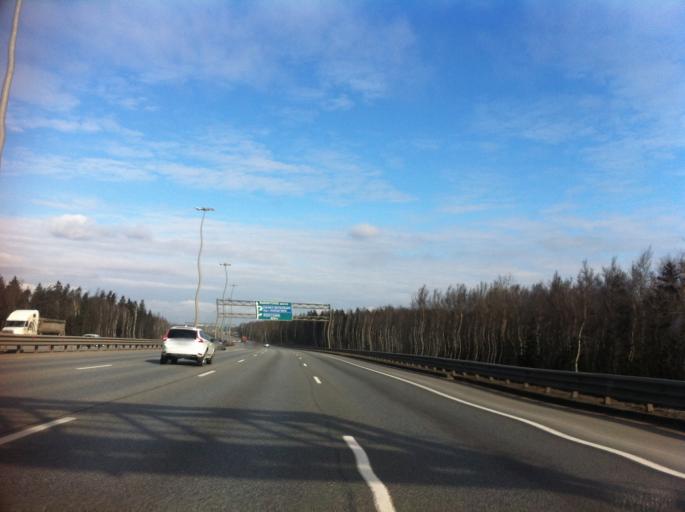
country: RU
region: St.-Petersburg
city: Krasnogvargeisky
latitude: 59.9330
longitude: 30.5378
